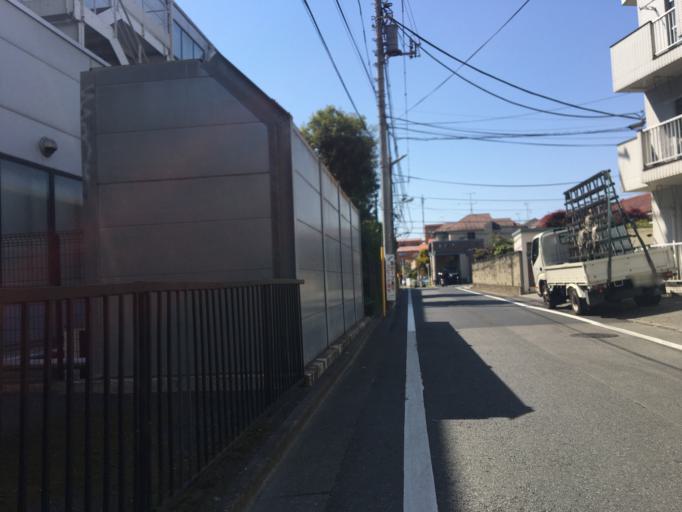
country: JP
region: Tokyo
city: Kokubunji
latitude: 35.7056
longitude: 139.4761
